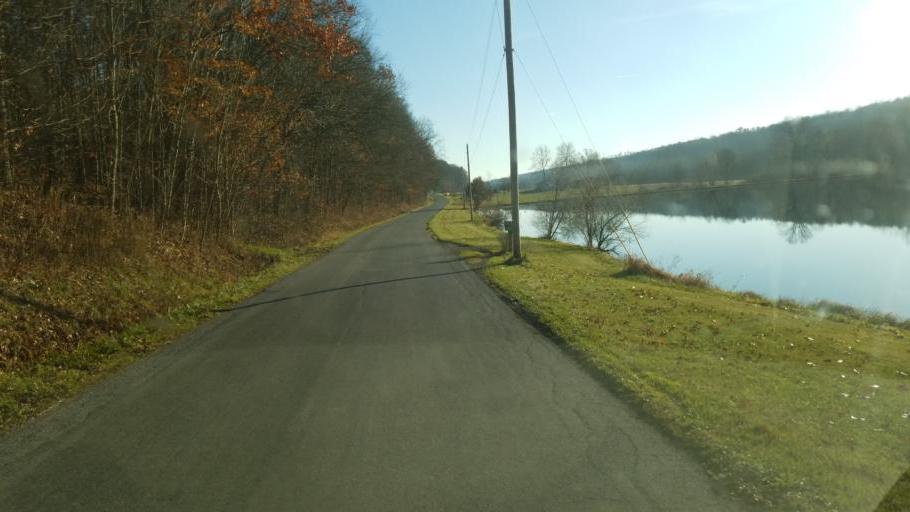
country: US
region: Ohio
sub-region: Wayne County
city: West Salem
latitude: 40.9079
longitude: -82.0065
